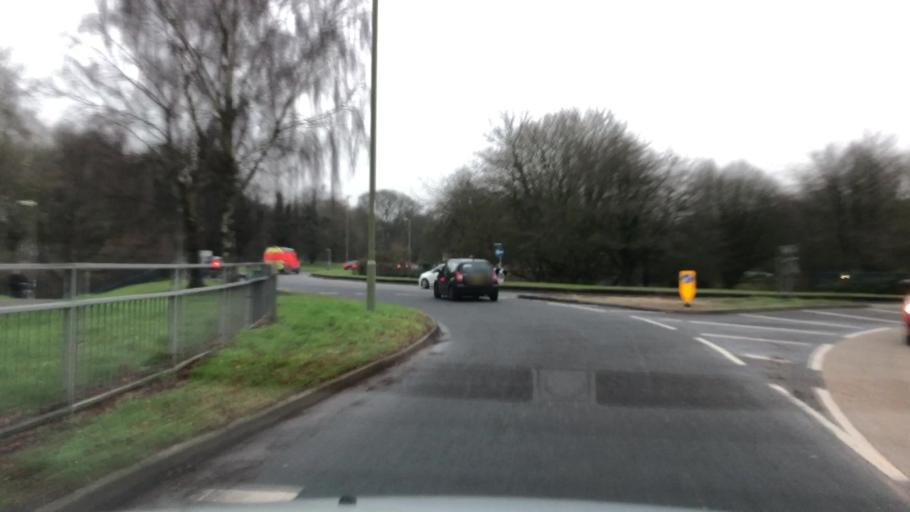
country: GB
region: England
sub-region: Hampshire
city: Basingstoke
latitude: 51.2489
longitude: -1.1000
